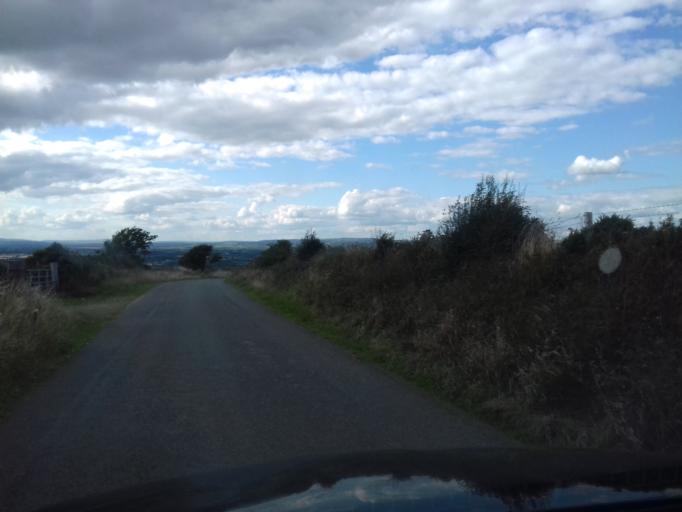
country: IE
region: Leinster
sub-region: Kilkenny
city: Graiguenamanagh
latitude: 52.5728
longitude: -7.0054
